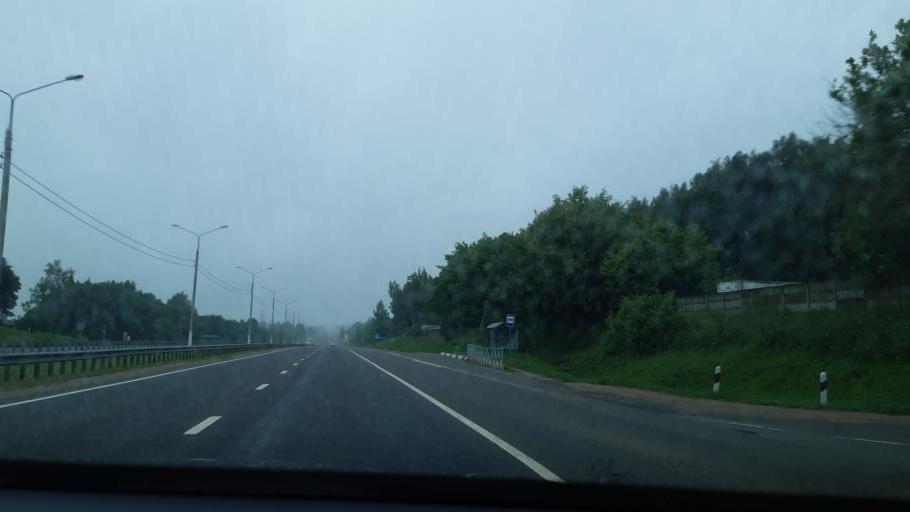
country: RU
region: Smolensk
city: Talashkino
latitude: 54.6500
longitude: 32.1687
